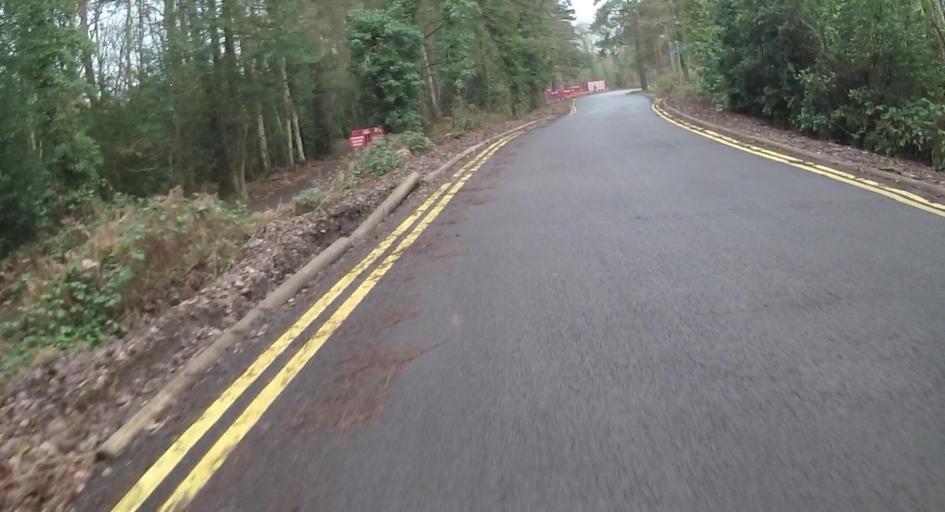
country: GB
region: England
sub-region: Wokingham
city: Finchampstead
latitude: 51.3771
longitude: -0.8711
